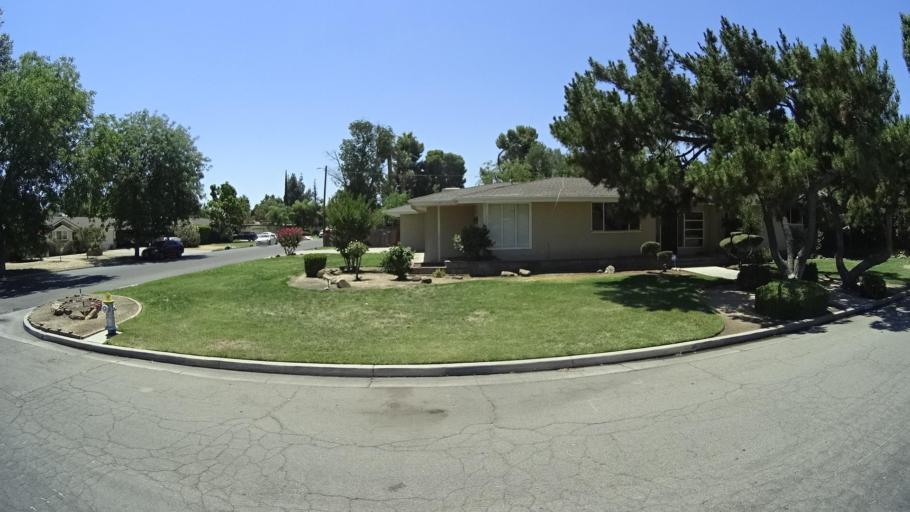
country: US
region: California
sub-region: Fresno County
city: Fresno
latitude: 36.7932
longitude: -119.7749
